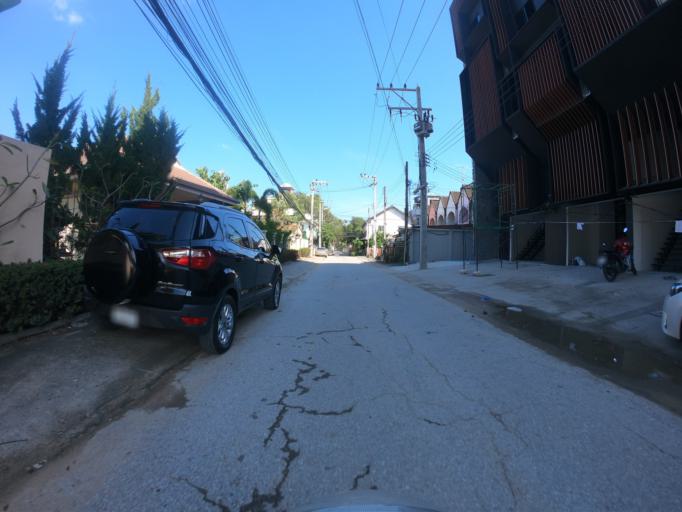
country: TH
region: Chiang Mai
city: Chiang Mai
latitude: 18.8051
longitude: 98.9739
